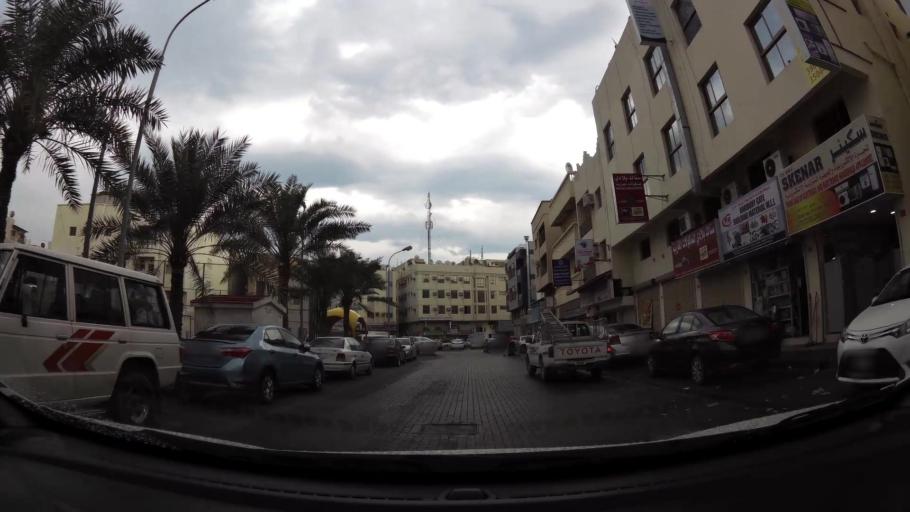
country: BH
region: Manama
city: Manama
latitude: 26.2300
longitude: 50.5902
